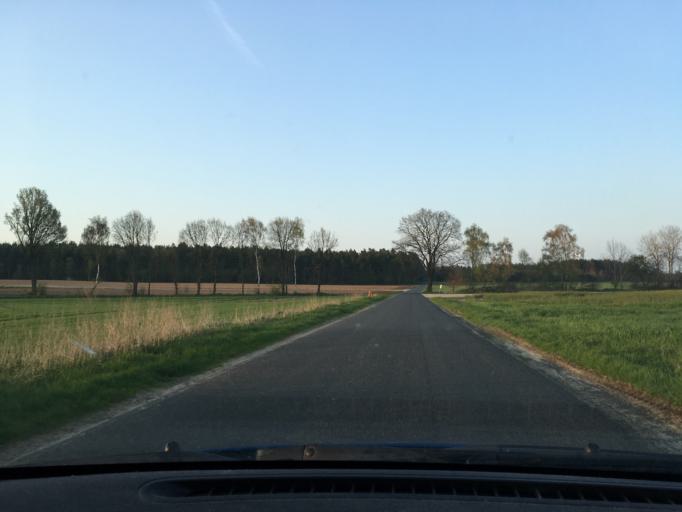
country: DE
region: Lower Saxony
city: Sudergellersen
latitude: 53.1866
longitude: 10.2687
